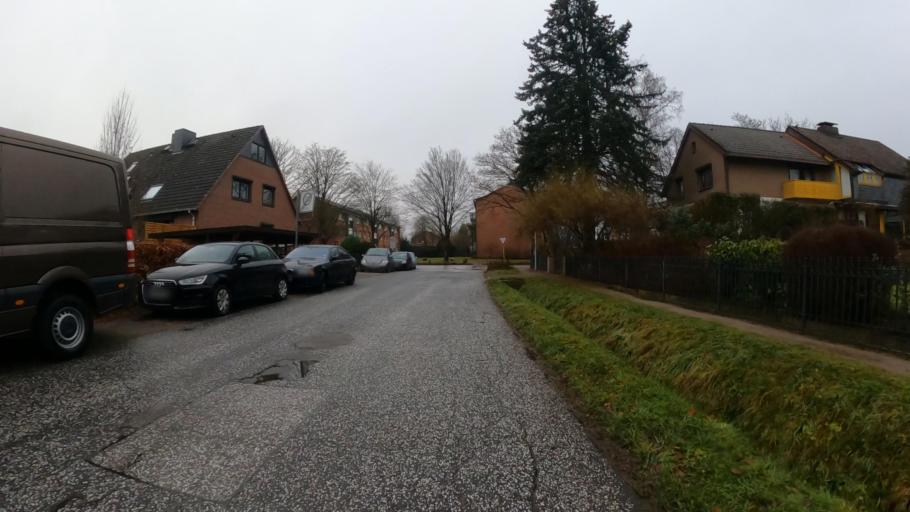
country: DE
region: Hamburg
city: Farmsen-Berne
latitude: 53.6181
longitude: 10.1474
